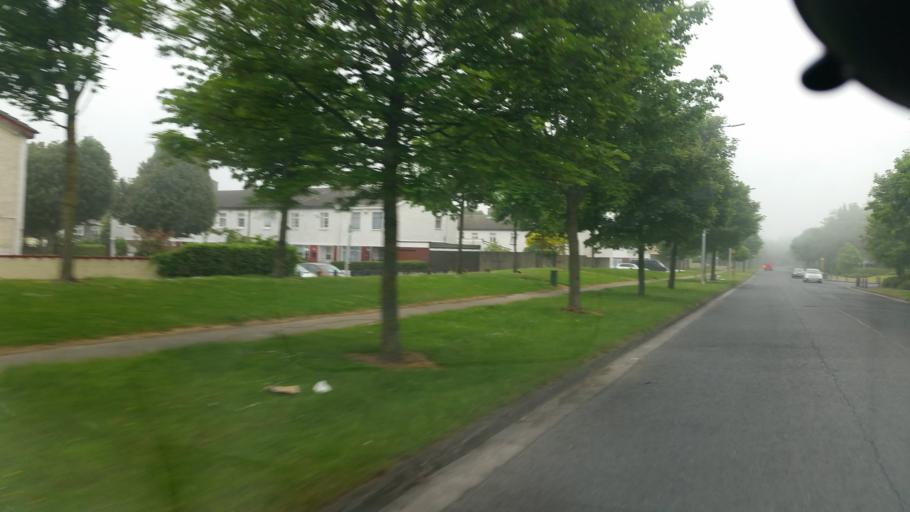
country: IE
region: Leinster
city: Ballymun
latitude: 53.4028
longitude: -6.2830
